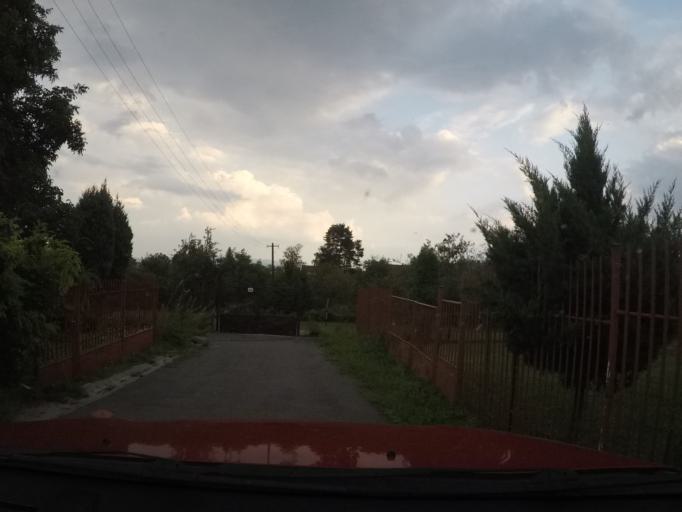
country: SK
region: Kosicky
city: Kosice
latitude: 48.6916
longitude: 21.2130
